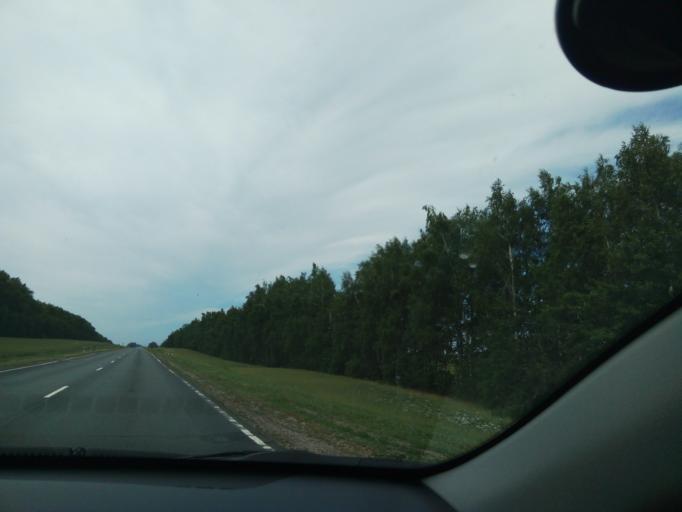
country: RU
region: Tambov
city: Selezni
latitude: 52.6402
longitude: 40.9627
